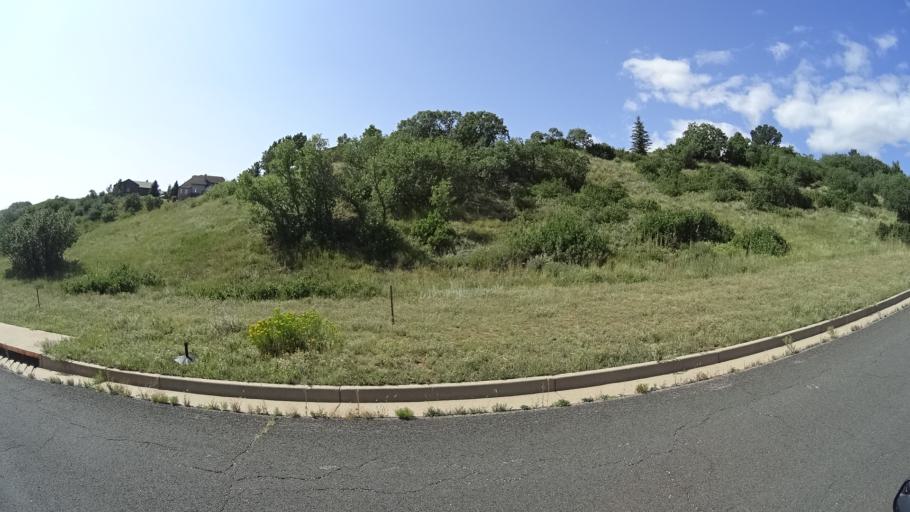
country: US
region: Colorado
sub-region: El Paso County
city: Manitou Springs
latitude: 38.9156
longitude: -104.8695
